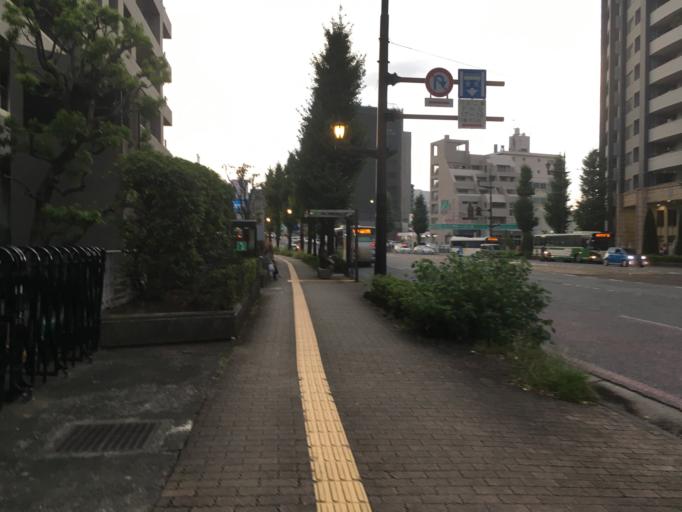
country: JP
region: Kumamoto
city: Kumamoto
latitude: 32.8002
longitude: 130.7169
